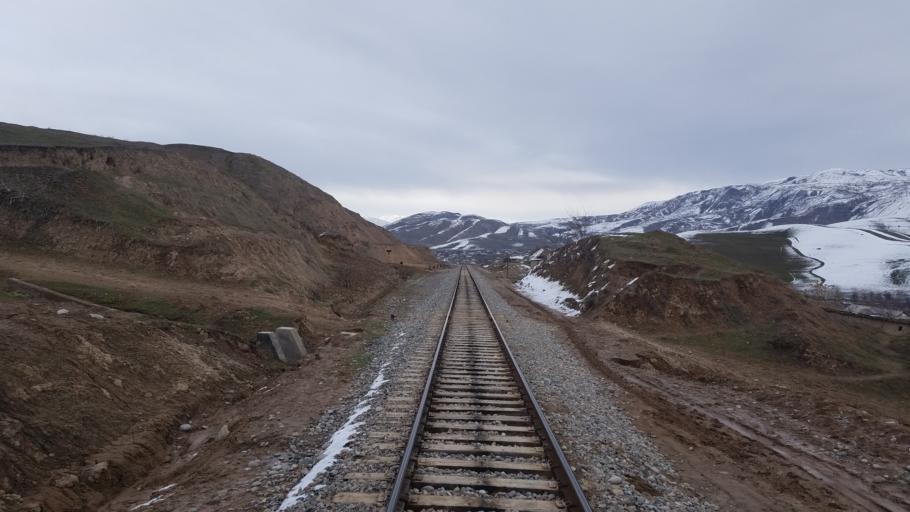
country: TJ
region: Republican Subordination
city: Vahdat
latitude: 38.4355
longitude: 68.9563
